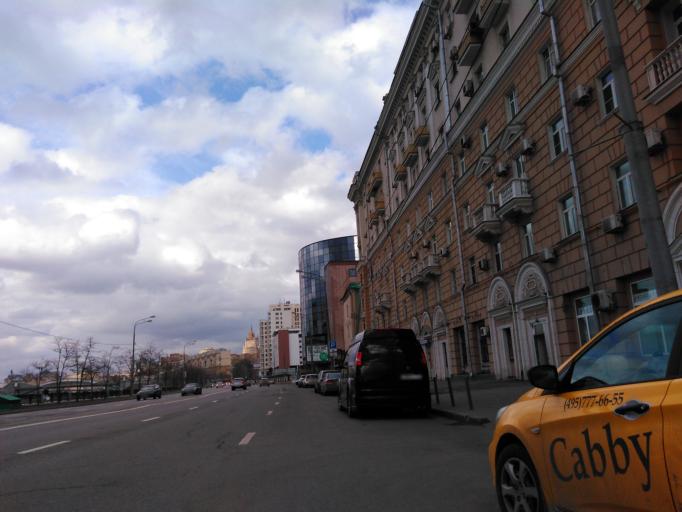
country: RU
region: Moskovskaya
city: Dorogomilovo
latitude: 55.7342
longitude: 37.5642
